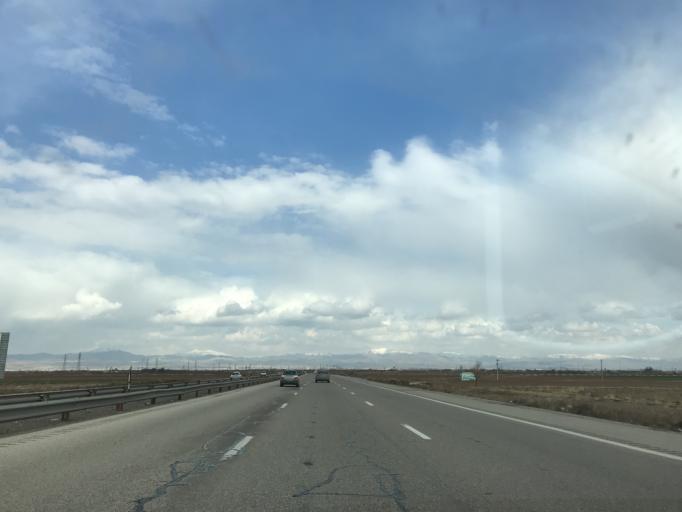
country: IR
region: Qazvin
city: Qazvin
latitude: 36.2360
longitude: 49.9050
